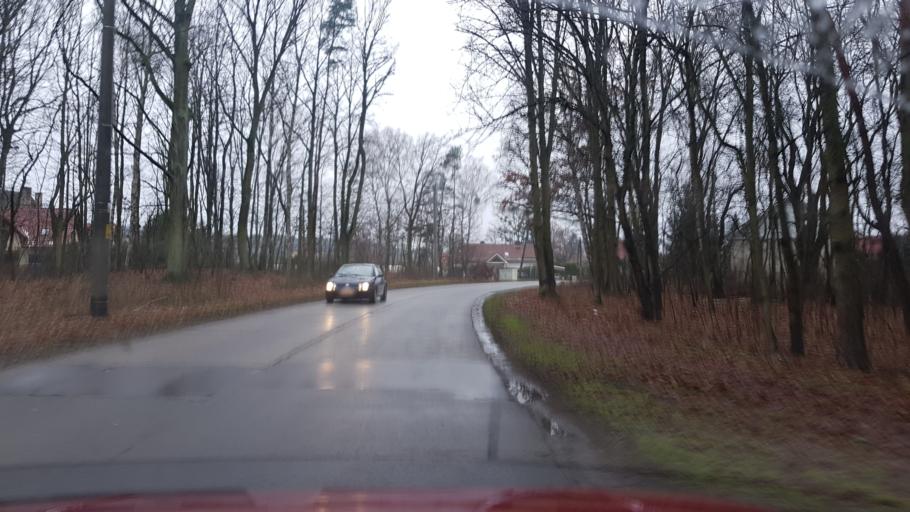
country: PL
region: West Pomeranian Voivodeship
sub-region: Powiat policki
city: Dobra
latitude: 53.5399
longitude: 14.4703
